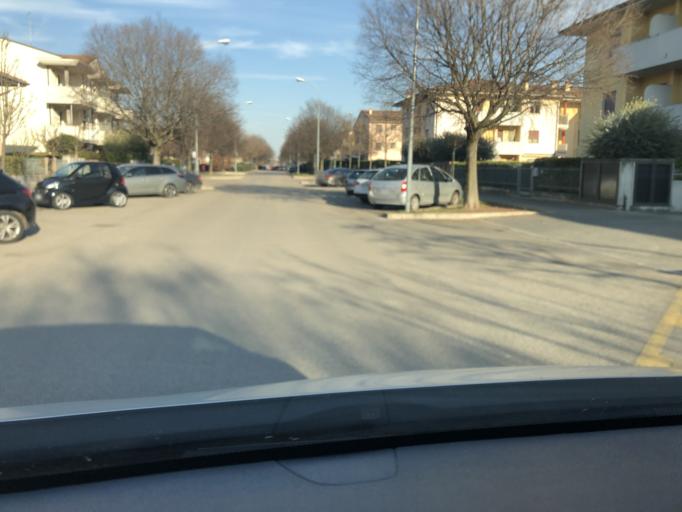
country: IT
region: Veneto
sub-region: Provincia di Verona
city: Caselle
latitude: 45.4141
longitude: 10.9010
